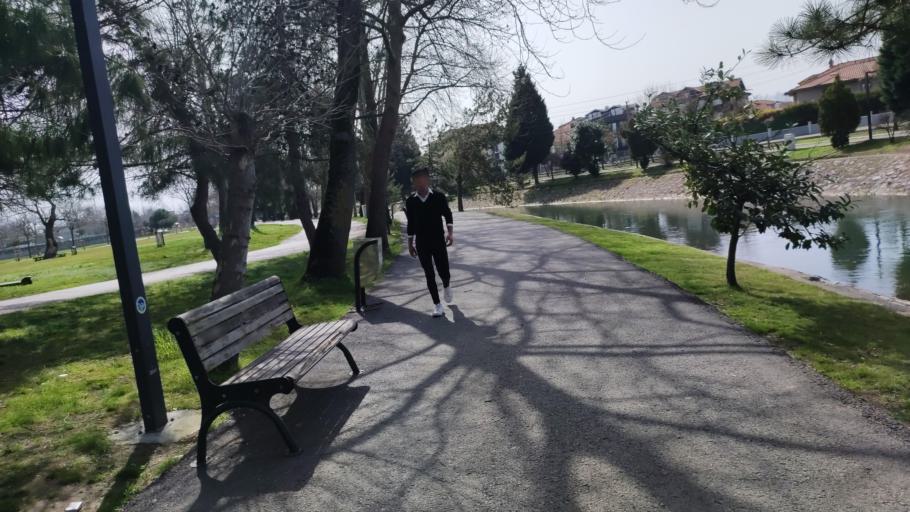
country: TR
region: Sakarya
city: Adapazari
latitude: 40.7745
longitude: 30.3854
